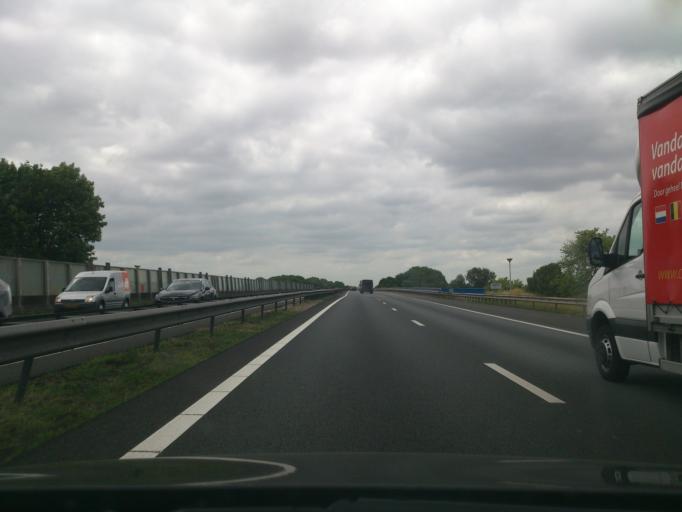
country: NL
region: North Brabant
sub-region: Gemeente Landerd
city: Reek
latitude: 51.7970
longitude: 5.6666
